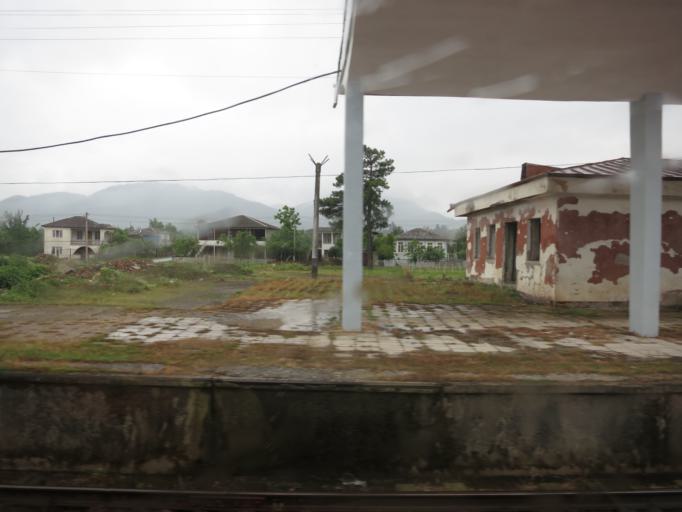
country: GE
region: Guria
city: Lanchkhuti
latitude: 42.0921
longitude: 42.0442
